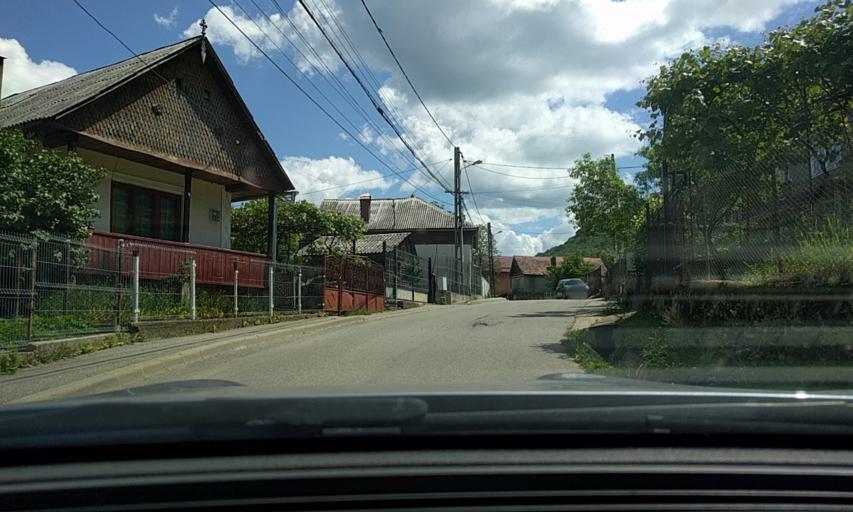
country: RO
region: Bistrita-Nasaud
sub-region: Oras Nasaud
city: Nasaud
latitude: 47.2774
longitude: 24.4068
